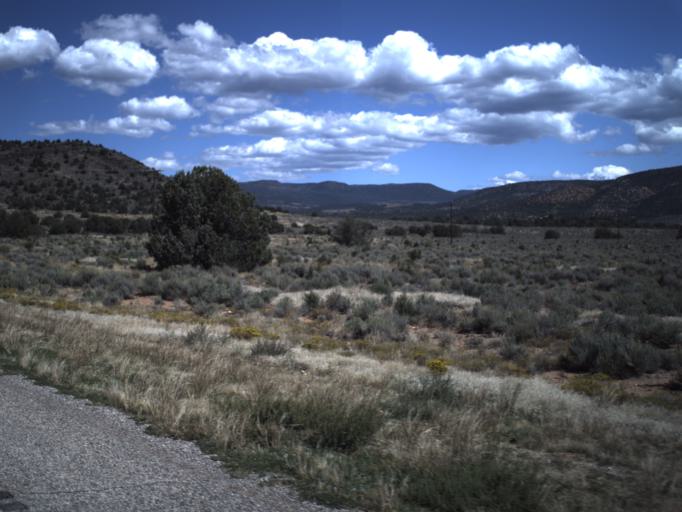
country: US
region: Utah
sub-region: Washington County
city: Enterprise
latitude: 37.3858
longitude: -113.6501
